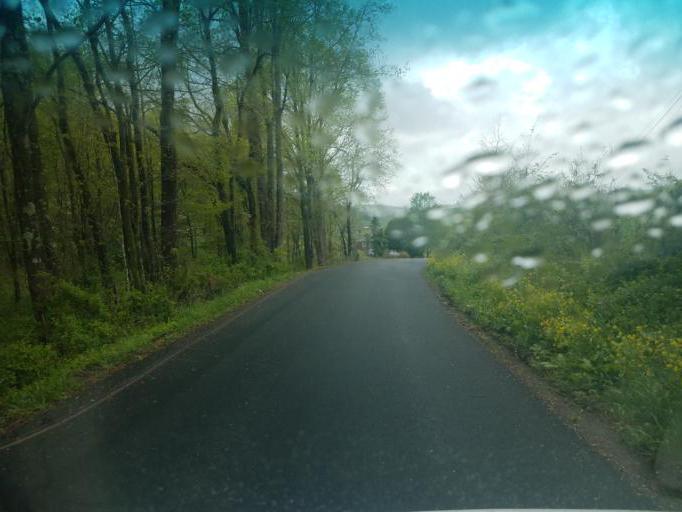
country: US
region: Virginia
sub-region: Smyth County
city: Marion
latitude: 36.9331
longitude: -81.5317
